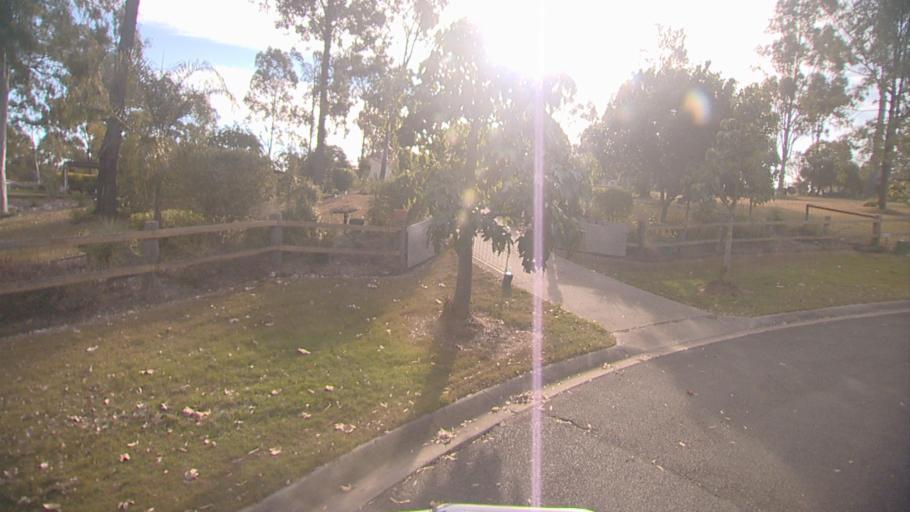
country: AU
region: Queensland
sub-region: Logan
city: North Maclean
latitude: -27.8026
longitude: 152.9640
